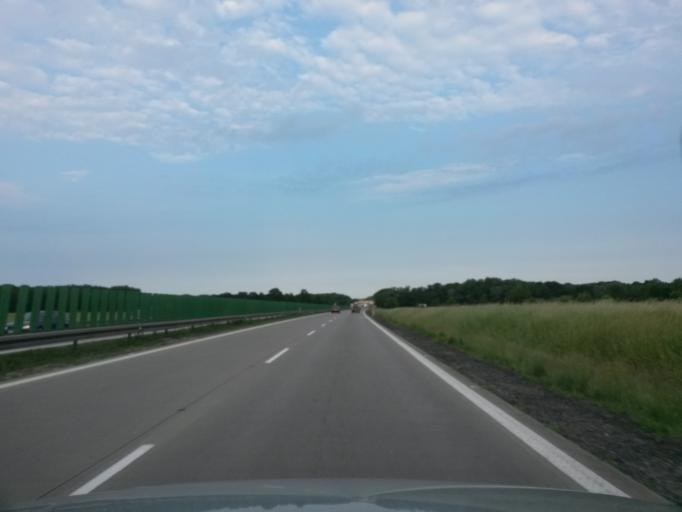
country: PL
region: Lower Silesian Voivodeship
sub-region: Powiat wroclawski
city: Katy Wroclawskie
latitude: 51.0275
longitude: 16.6625
